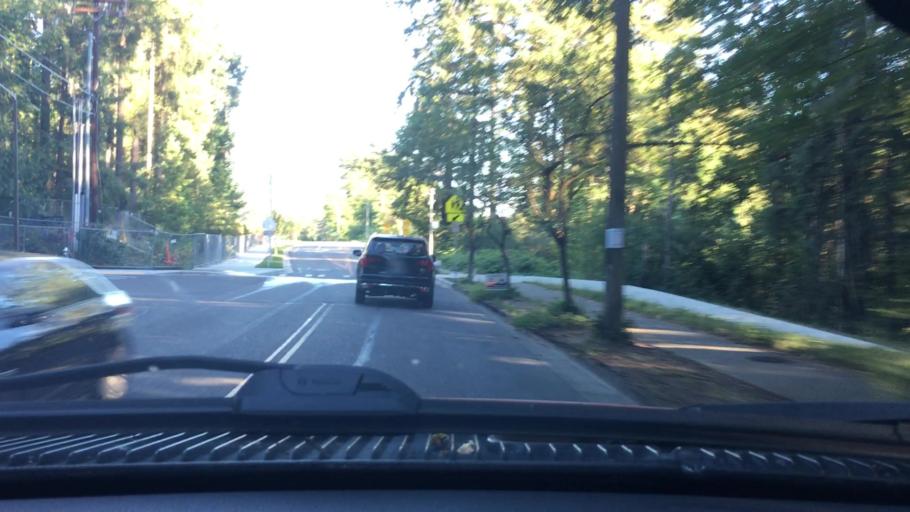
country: US
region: Washington
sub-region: King County
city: Issaquah
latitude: 47.5257
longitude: -122.0326
